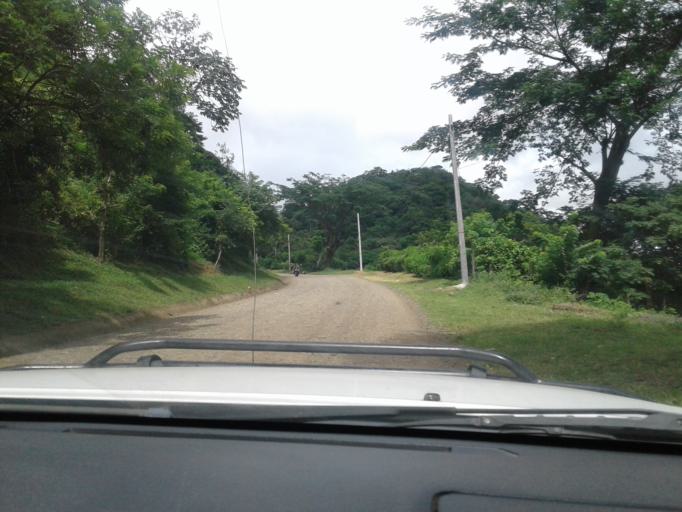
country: NI
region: Matagalpa
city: San Ramon
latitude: 12.9144
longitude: -85.8121
